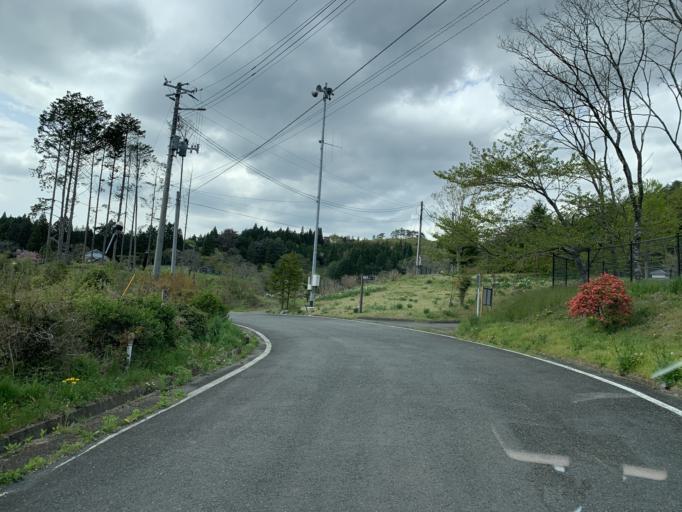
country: JP
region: Iwate
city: Ichinoseki
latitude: 38.7927
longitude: 141.4048
